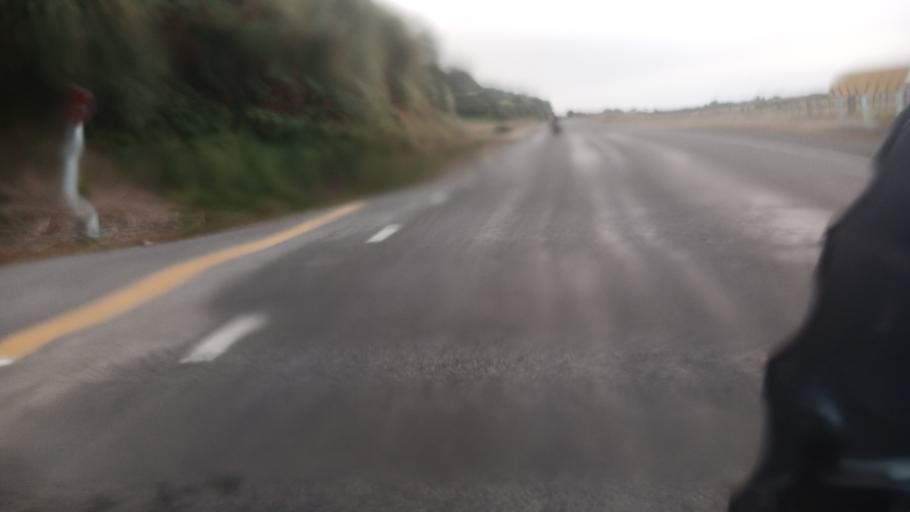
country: NZ
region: Bay of Plenty
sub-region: Opotiki District
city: Opotiki
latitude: -37.9849
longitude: 177.4073
